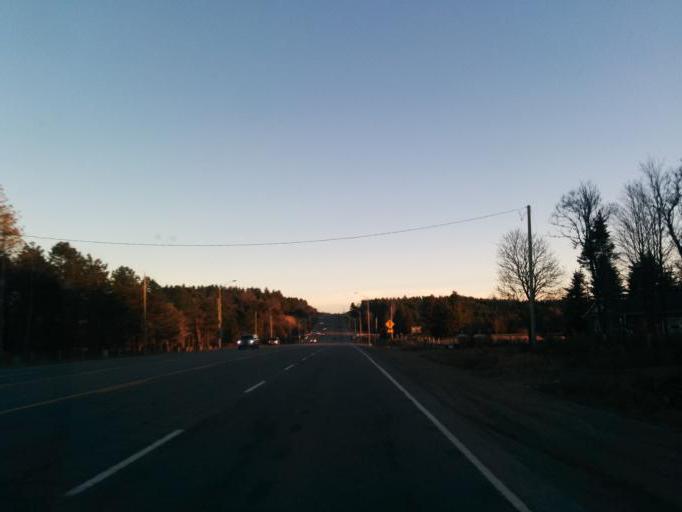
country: CA
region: Ontario
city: Orangeville
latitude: 43.9040
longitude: -80.0557
